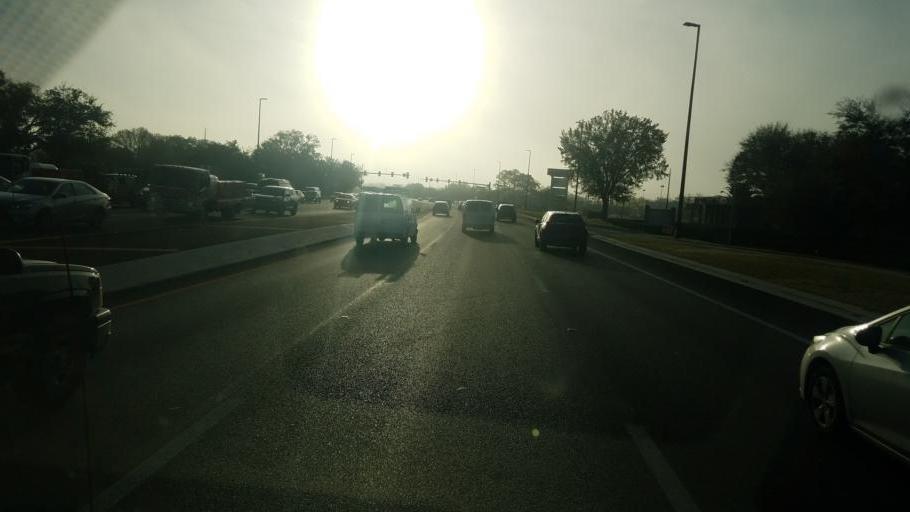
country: US
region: Florida
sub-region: Osceola County
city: Saint Cloud
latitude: 28.2484
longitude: -81.3092
